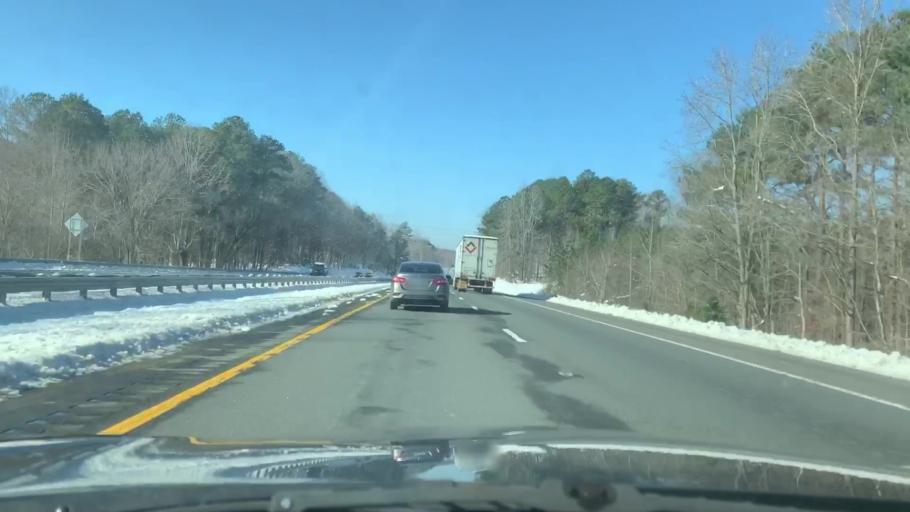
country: US
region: North Carolina
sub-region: Orange County
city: Hillsborough
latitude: 36.0389
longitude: -79.0197
